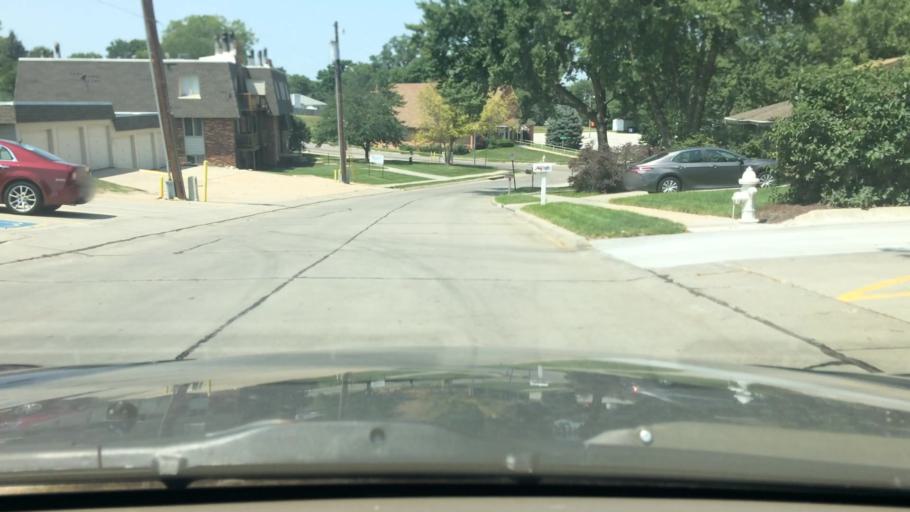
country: US
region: Nebraska
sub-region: Sarpy County
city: La Vista
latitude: 41.1922
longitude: -96.0411
